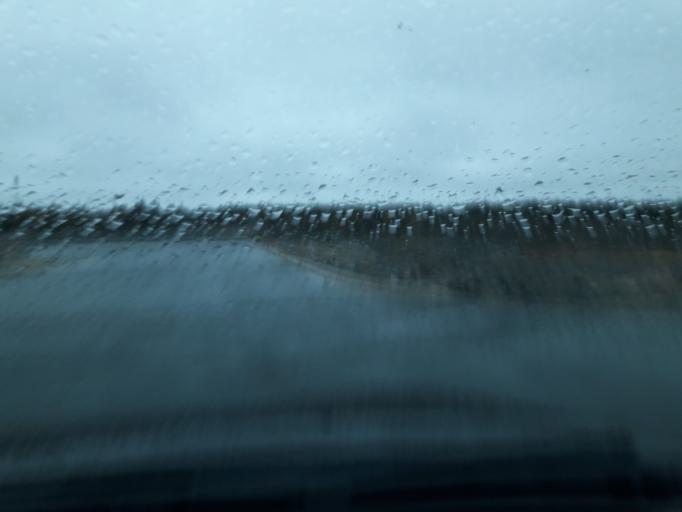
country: CA
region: Newfoundland and Labrador
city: Mount Pearl
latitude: 47.5580
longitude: -52.8037
